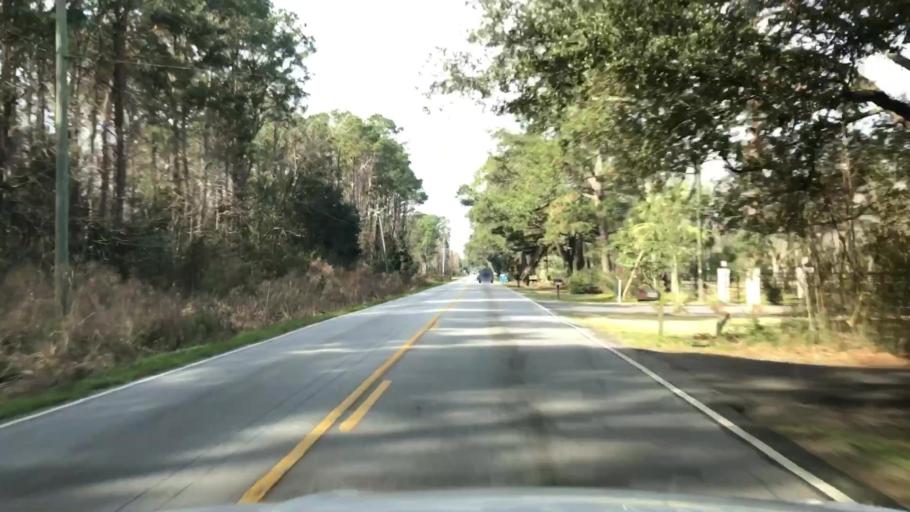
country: US
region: South Carolina
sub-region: Charleston County
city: Shell Point
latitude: 32.7690
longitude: -80.0742
